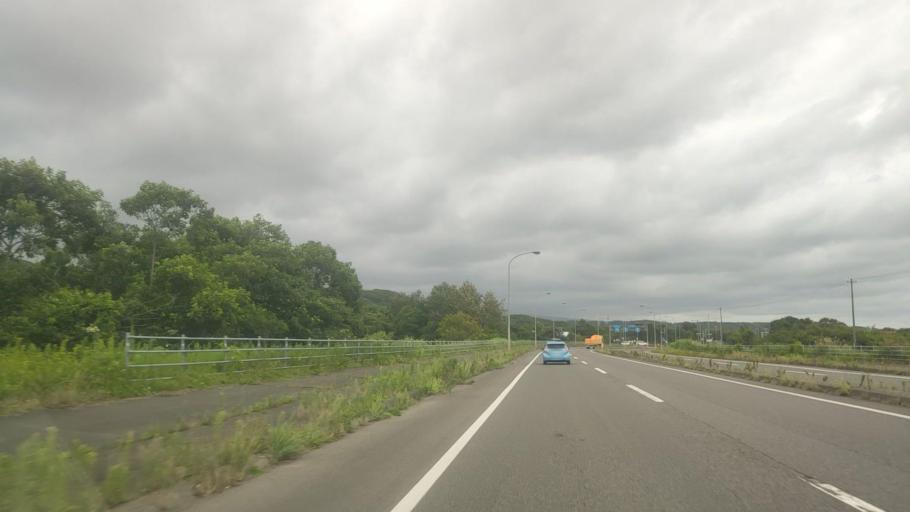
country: JP
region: Hokkaido
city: Shiraoi
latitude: 42.5613
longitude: 141.3808
